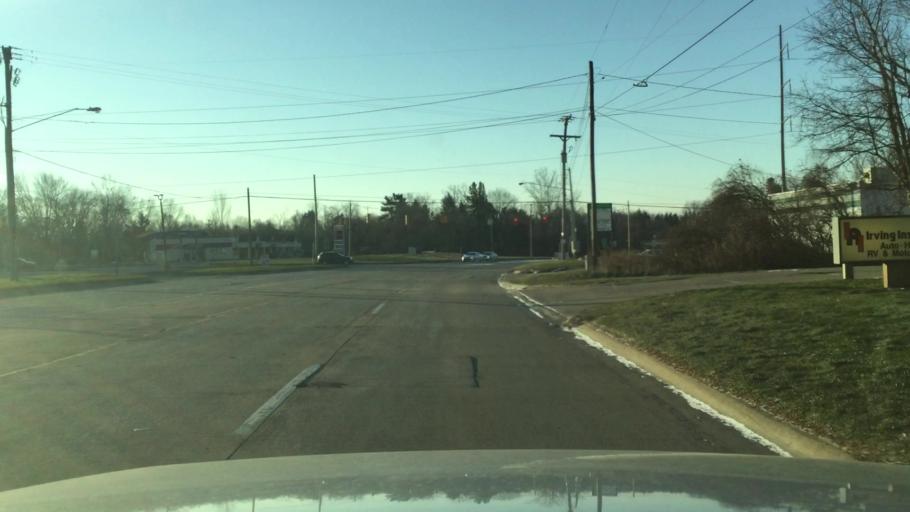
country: US
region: Michigan
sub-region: Genesee County
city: Flushing
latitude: 43.0470
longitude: -83.7728
